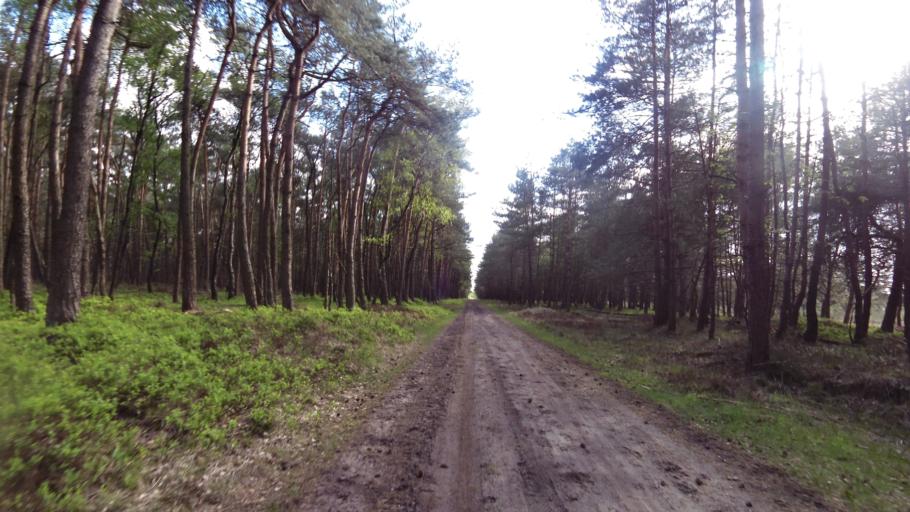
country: NL
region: Gelderland
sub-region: Gemeente Rozendaal
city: Rozendaal
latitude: 52.0687
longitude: 5.9508
